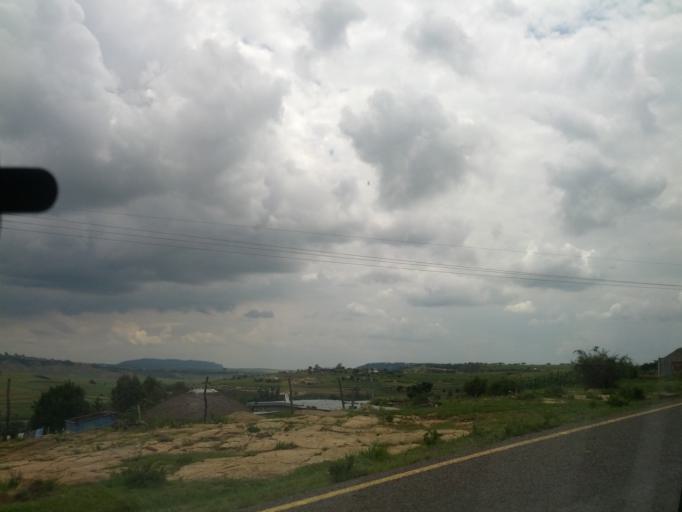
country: LS
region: Leribe
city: Leribe
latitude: -28.9690
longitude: 28.1726
